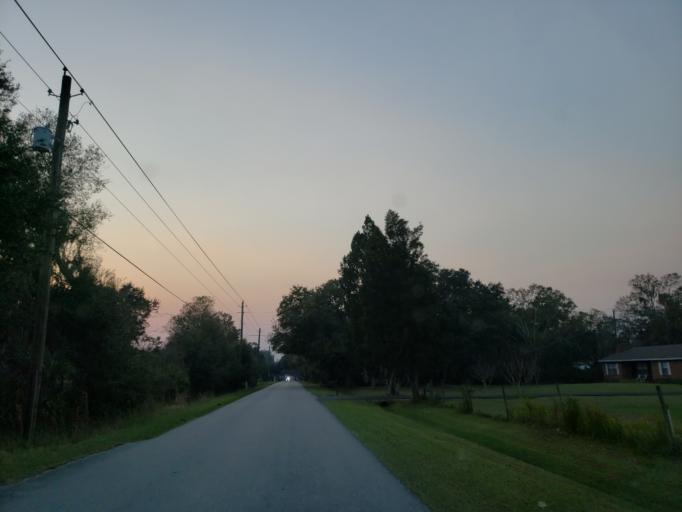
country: US
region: Florida
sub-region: Hillsborough County
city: Fish Hawk
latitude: 27.8428
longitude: -82.1962
